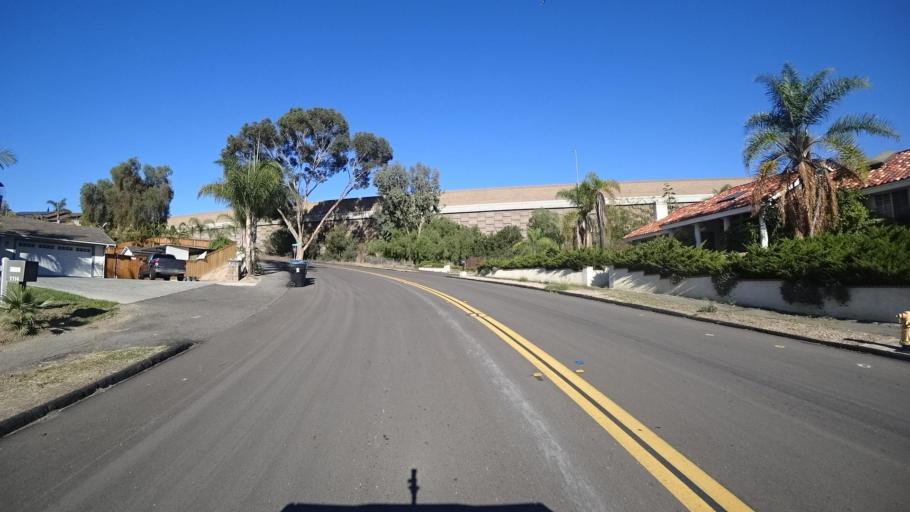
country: US
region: California
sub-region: San Diego County
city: Bonita
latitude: 32.6865
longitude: -117.0217
